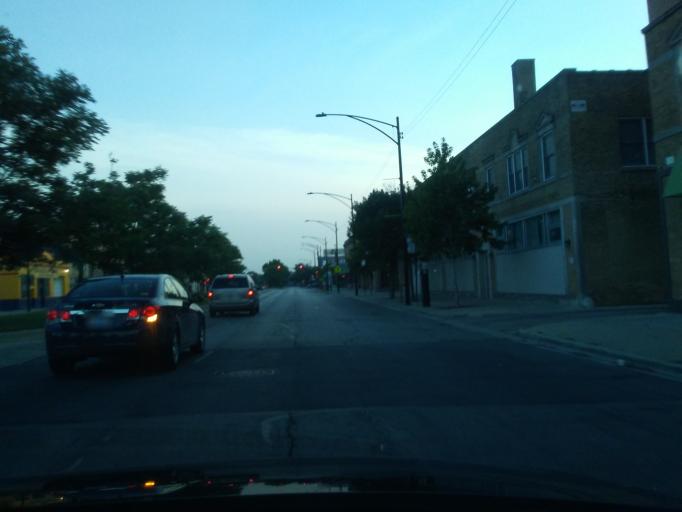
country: US
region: Illinois
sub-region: Cook County
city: Evanston
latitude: 41.9930
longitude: -87.6700
